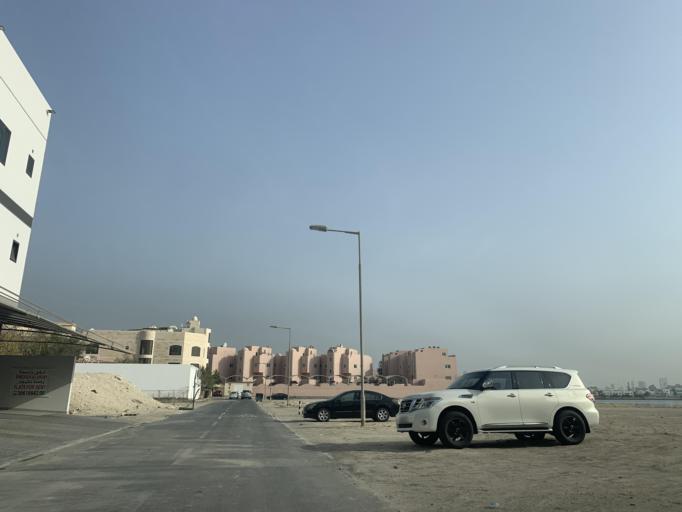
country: BH
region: Northern
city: Madinat `Isa
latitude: 26.1920
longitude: 50.5657
